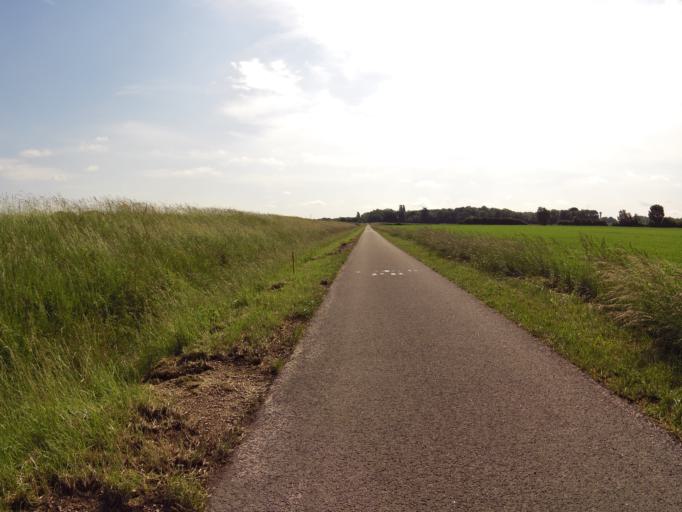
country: FR
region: Champagne-Ardenne
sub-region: Departement de l'Aube
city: Saint-Julien-les-Villas
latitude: 48.2653
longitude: 4.1238
